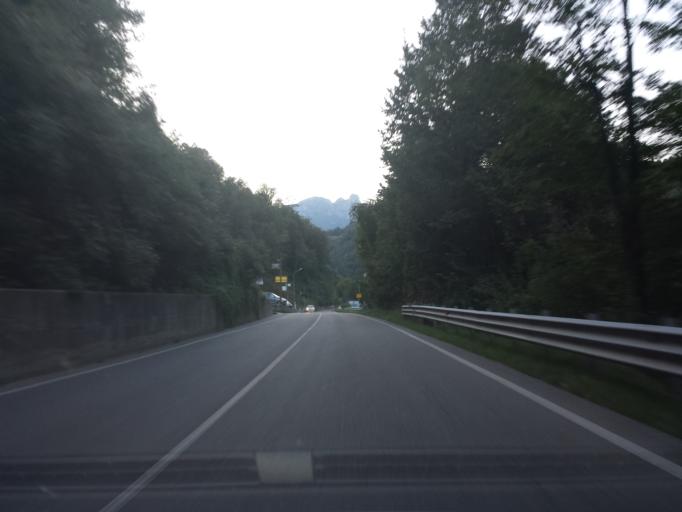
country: IT
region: Veneto
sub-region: Provincia di Vicenza
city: Recoaro Terme
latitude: 45.7012
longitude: 11.2471
